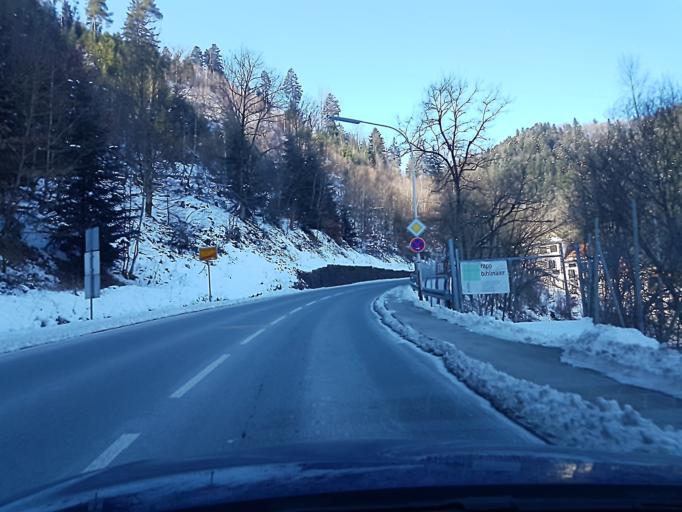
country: DE
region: Baden-Wuerttemberg
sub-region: Freiburg Region
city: Schramberg
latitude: 48.2212
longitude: 8.3770
